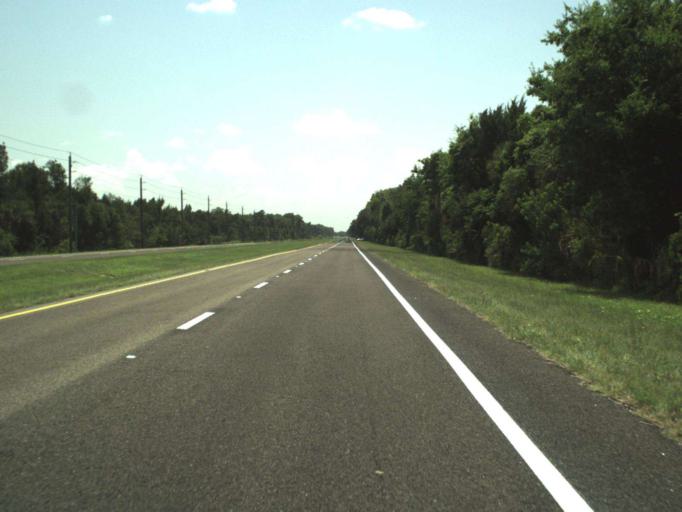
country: US
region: Florida
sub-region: Volusia County
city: Oak Hill
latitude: 28.8185
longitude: -80.8623
